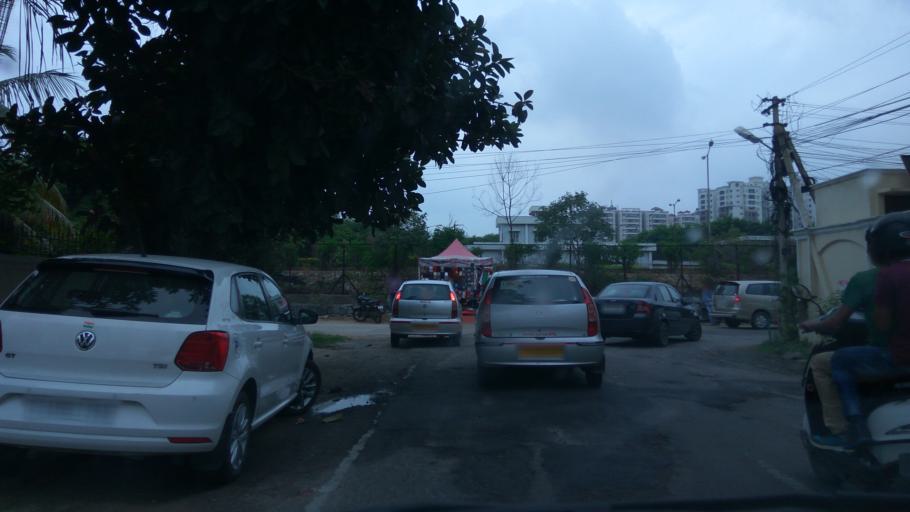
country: IN
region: Telangana
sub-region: Rangareddi
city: Kukatpalli
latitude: 17.4363
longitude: 78.3929
